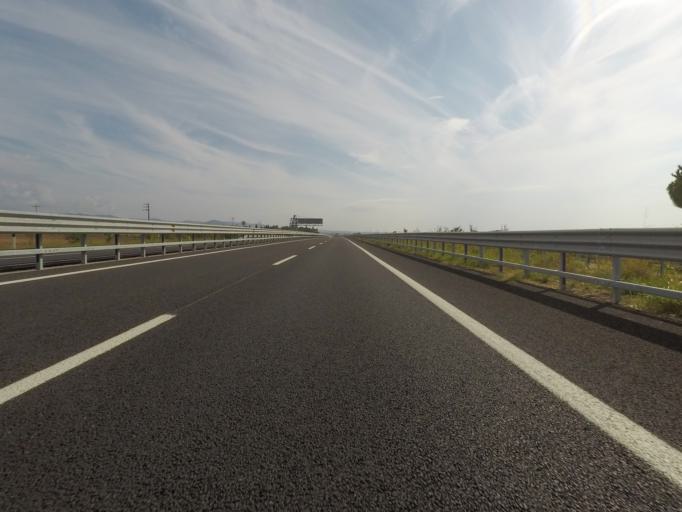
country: IT
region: Latium
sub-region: Provincia di Viterbo
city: Tarquinia
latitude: 42.2243
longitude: 11.7694
